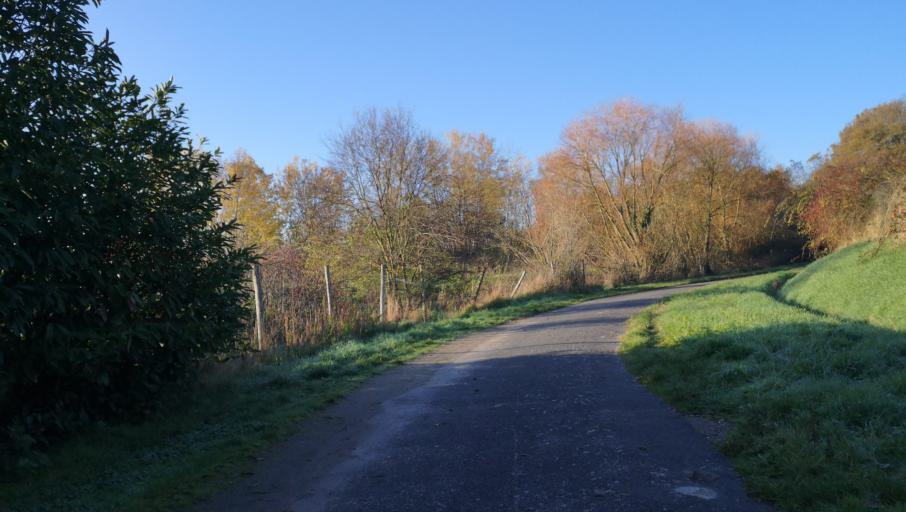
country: FR
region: Centre
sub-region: Departement du Loiret
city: Saran
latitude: 47.9421
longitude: 1.8628
